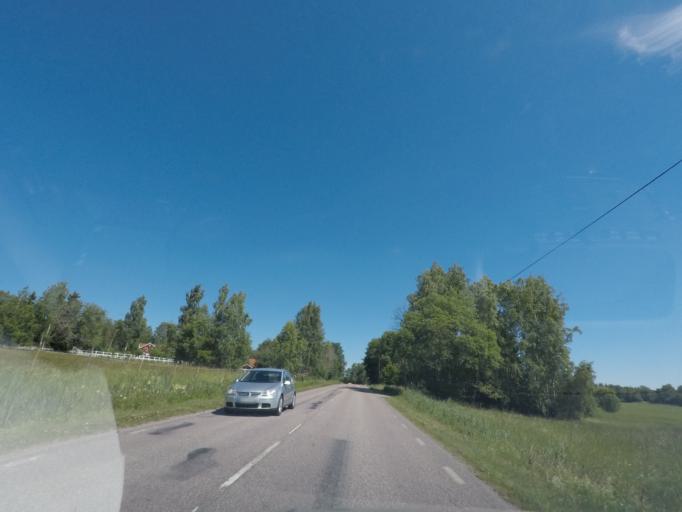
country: SE
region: Vaestmanland
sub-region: Vasteras
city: Tillberga
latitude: 59.6390
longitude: 16.6752
